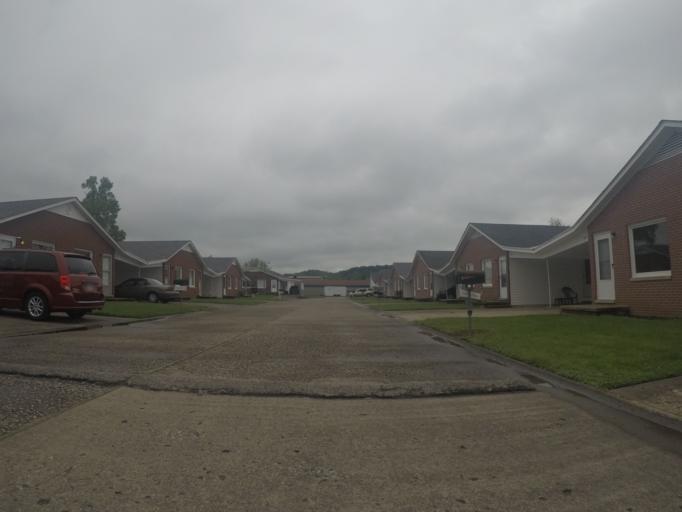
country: US
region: West Virginia
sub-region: Cabell County
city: Barboursville
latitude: 38.4132
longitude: -82.3011
